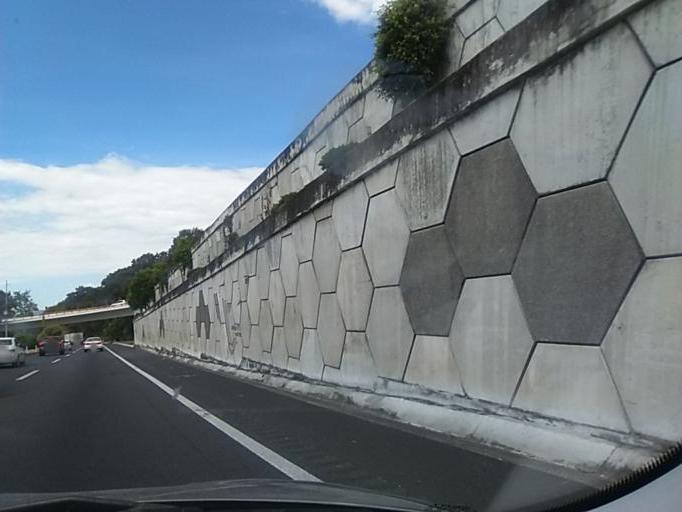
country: MX
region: Morelos
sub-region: Cuernavaca
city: Villa Santiago
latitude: 19.0097
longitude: -99.1723
